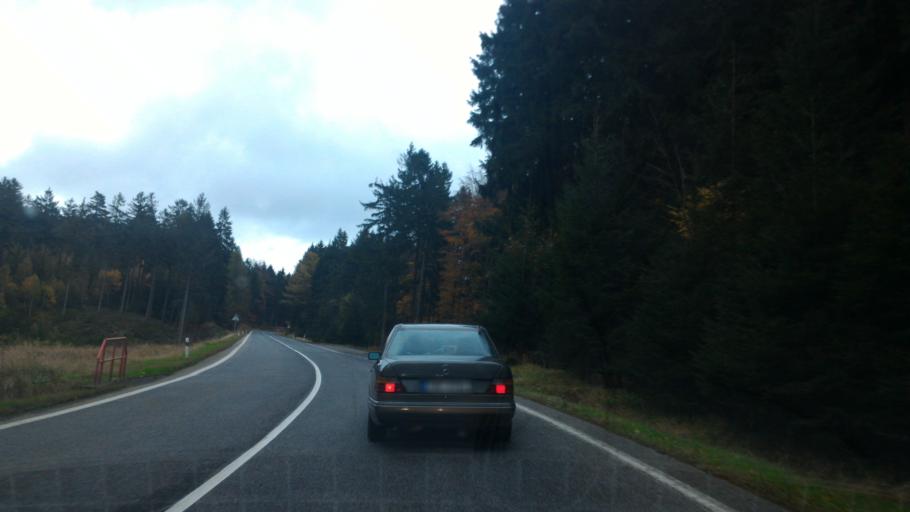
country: CZ
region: Ustecky
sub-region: Okres Decin
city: Chribska
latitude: 50.8366
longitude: 14.4864
